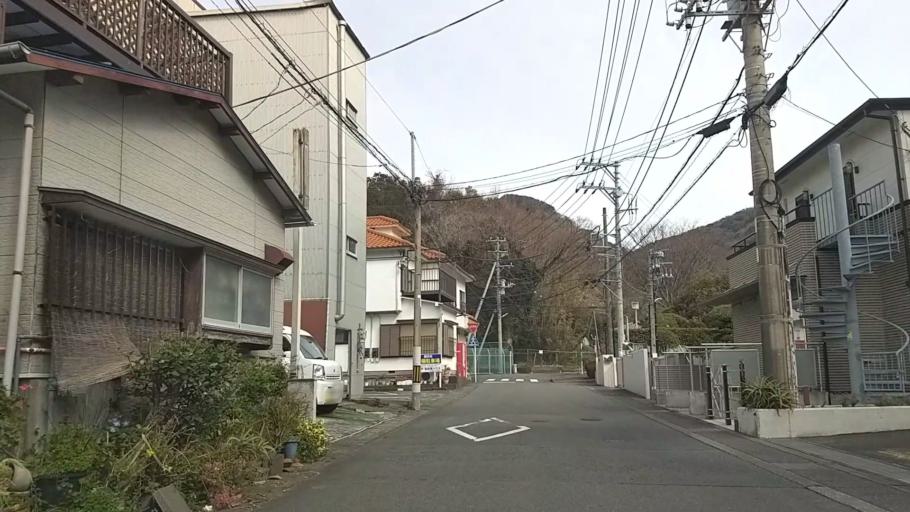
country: JP
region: Shizuoka
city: Shimoda
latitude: 34.6823
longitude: 138.9495
